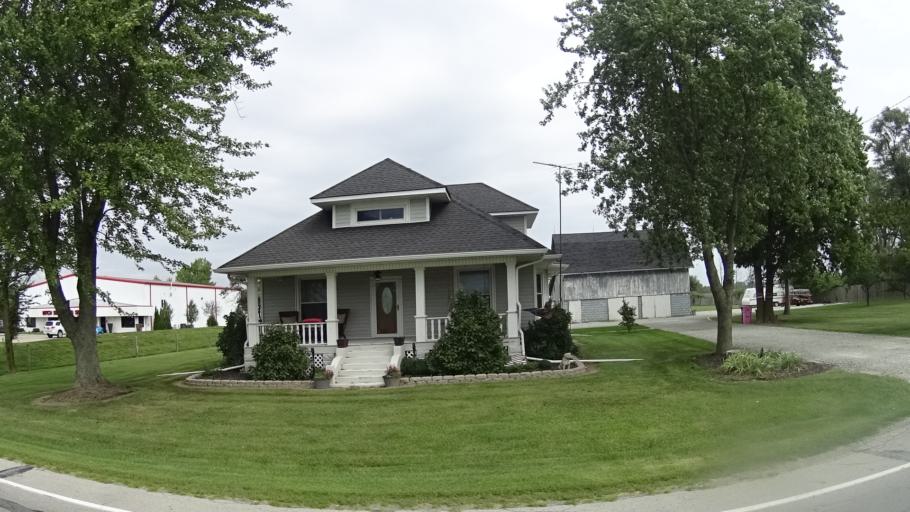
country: US
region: Indiana
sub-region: Madison County
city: Edgewood
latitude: 40.1012
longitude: -85.7588
